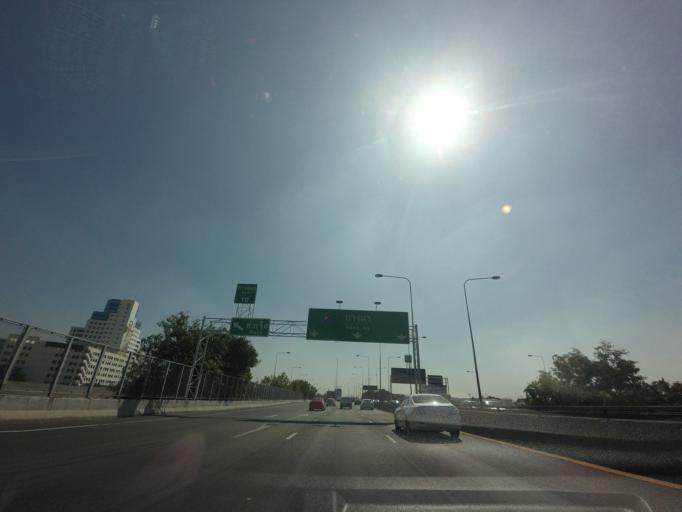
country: TH
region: Bangkok
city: Khlong Toei
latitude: 13.7132
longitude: 100.5608
